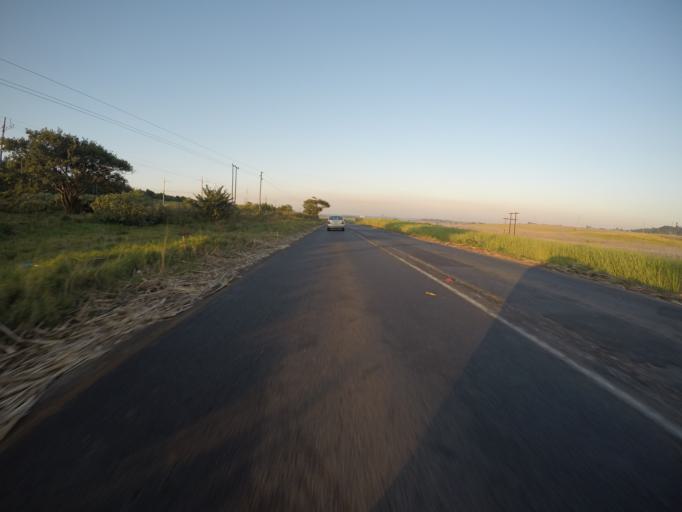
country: ZA
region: KwaZulu-Natal
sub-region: uThungulu District Municipality
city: Empangeni
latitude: -28.8053
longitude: 31.8927
